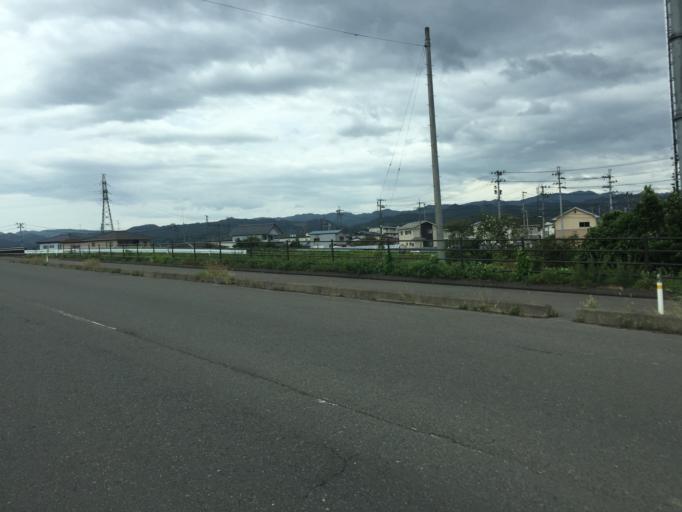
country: JP
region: Fukushima
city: Yanagawamachi-saiwaicho
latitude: 37.8561
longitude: 140.5953
